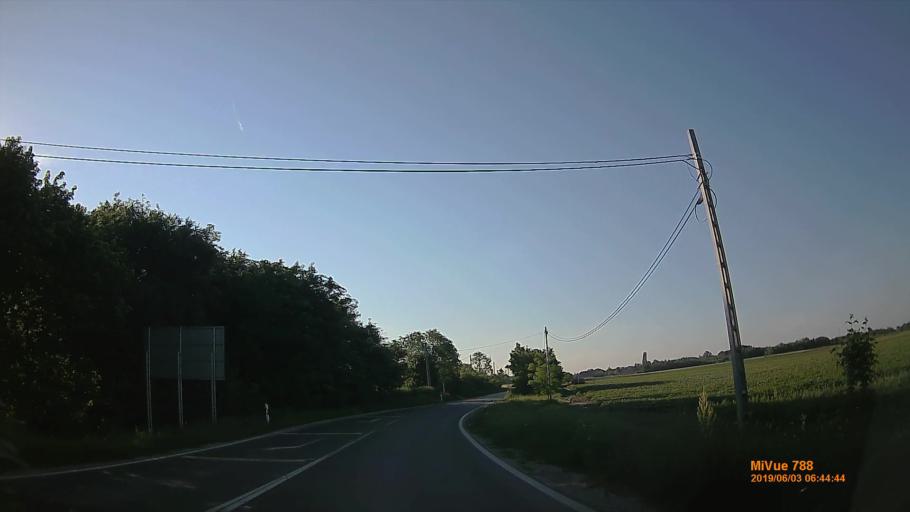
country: HU
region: Pest
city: Bugyi
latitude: 47.2431
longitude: 19.1291
